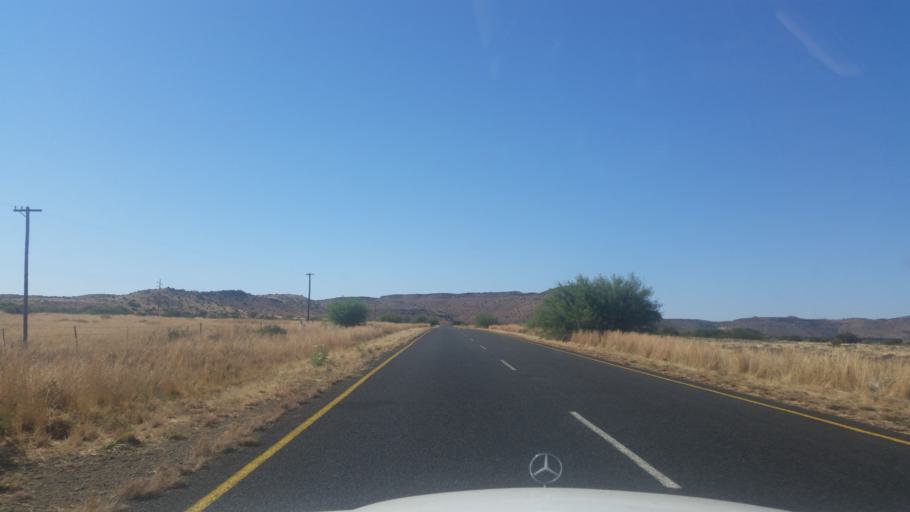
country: ZA
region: Orange Free State
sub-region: Xhariep District Municipality
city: Trompsburg
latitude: -30.5027
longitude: 26.0112
